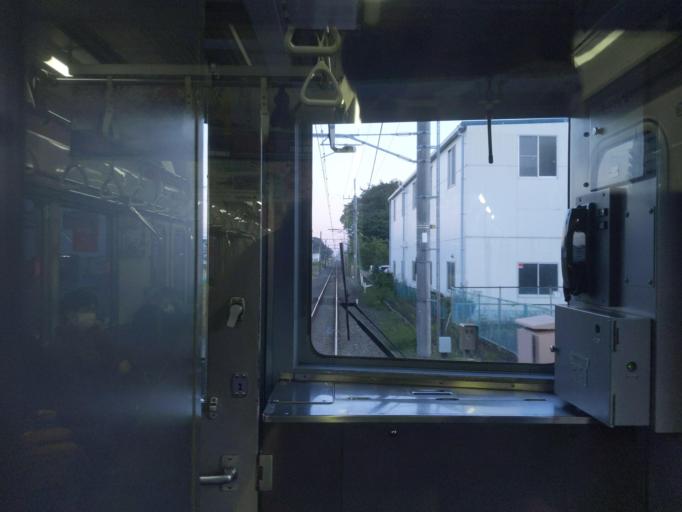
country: JP
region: Chiba
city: Noda
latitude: 35.9299
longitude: 139.8926
